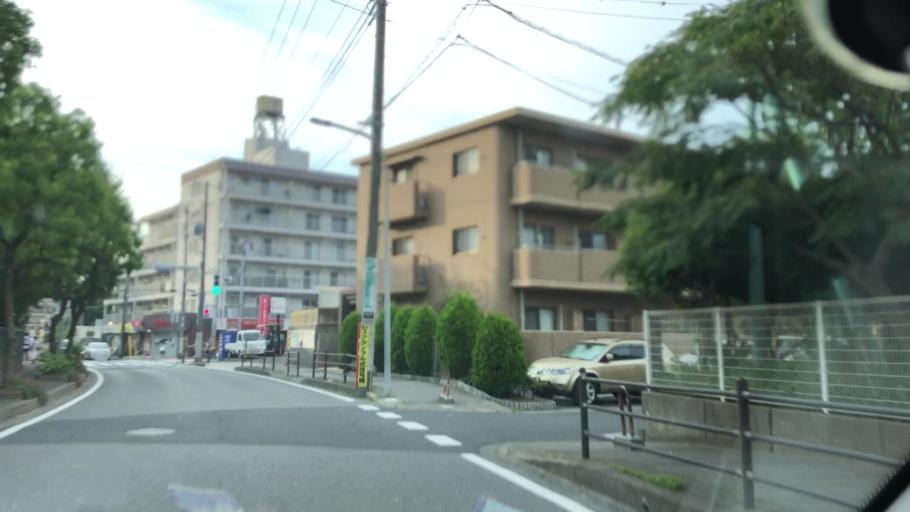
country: JP
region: Tokyo
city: Urayasu
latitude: 35.6719
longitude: 139.9062
